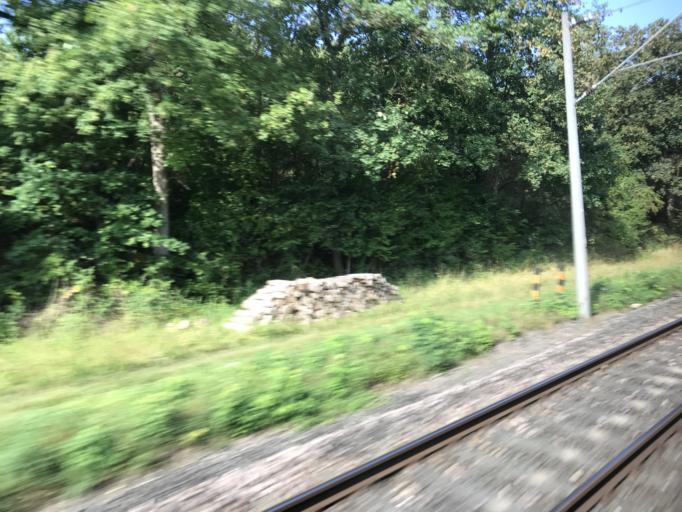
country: DE
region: Hesse
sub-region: Regierungsbezirk Giessen
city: Runkel
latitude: 50.3672
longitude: 8.1385
